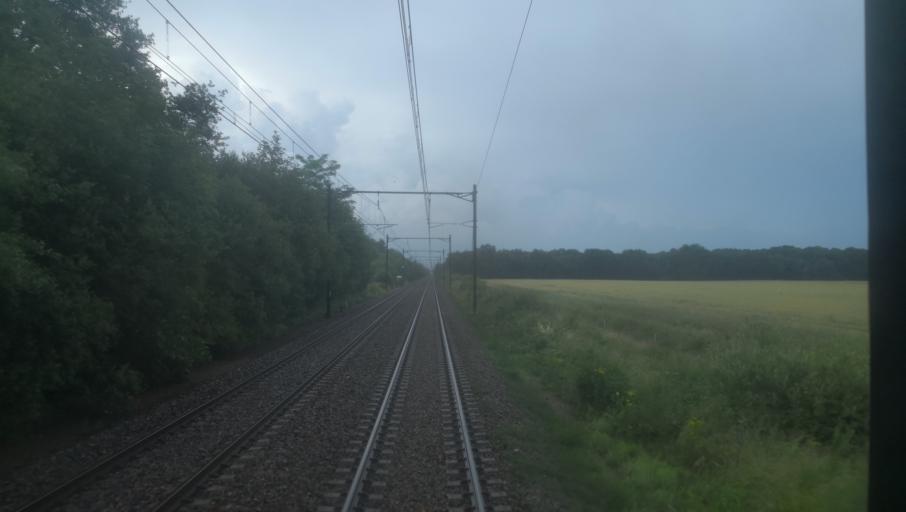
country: FR
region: Centre
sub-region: Departement du Loiret
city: La Ferte-Saint-Aubin
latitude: 47.7713
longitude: 1.9382
